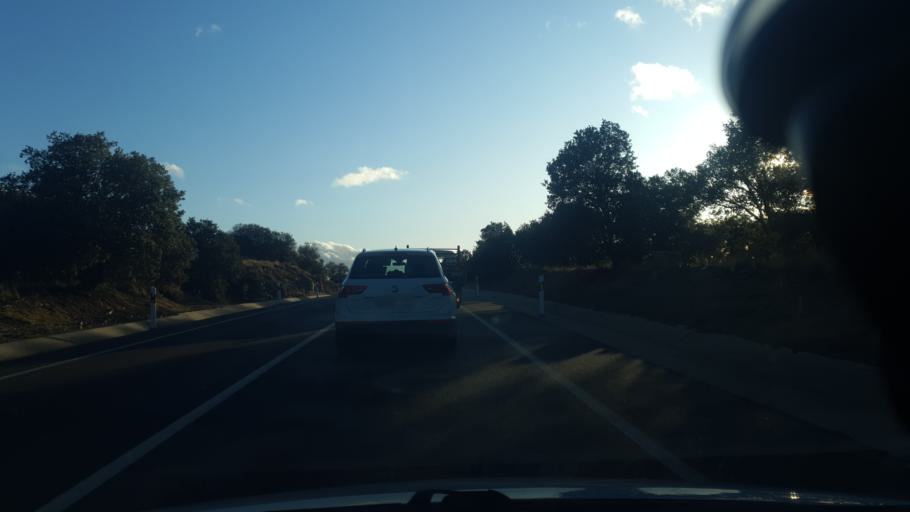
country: ES
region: Castille and Leon
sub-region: Provincia de Avila
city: Mingorria
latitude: 40.7191
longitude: -4.6733
